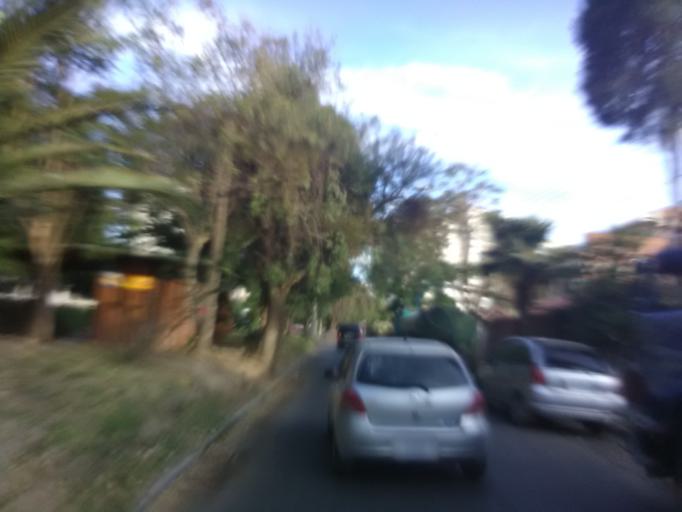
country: BO
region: Cochabamba
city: Cochabamba
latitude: -17.3714
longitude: -66.1523
